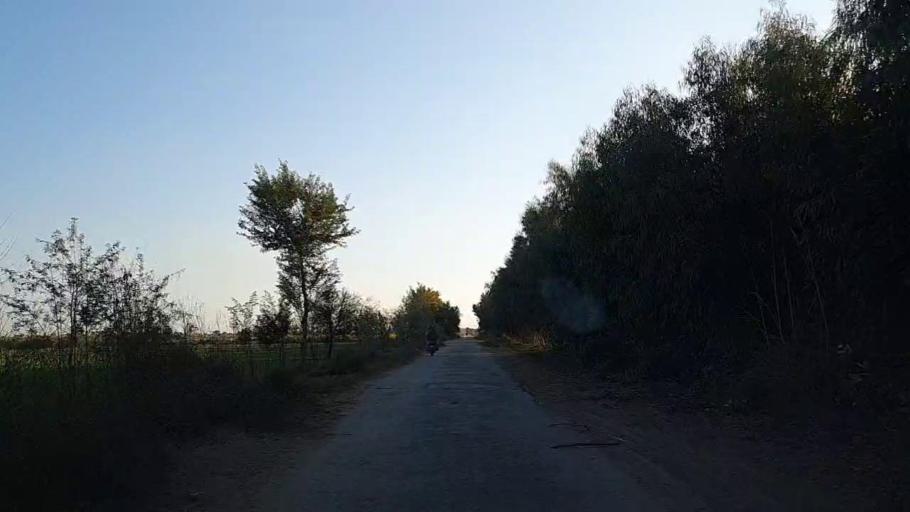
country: PK
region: Sindh
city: Khadro
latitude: 26.2752
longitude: 68.8100
